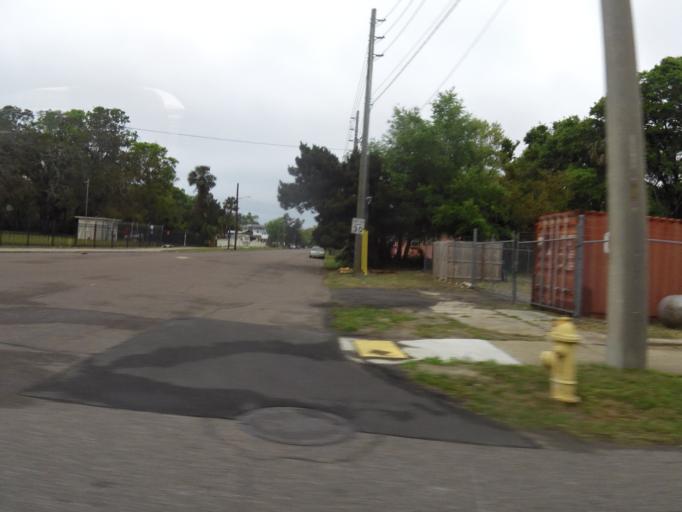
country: US
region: Florida
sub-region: Duval County
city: Jacksonville
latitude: 30.3313
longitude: -81.6470
